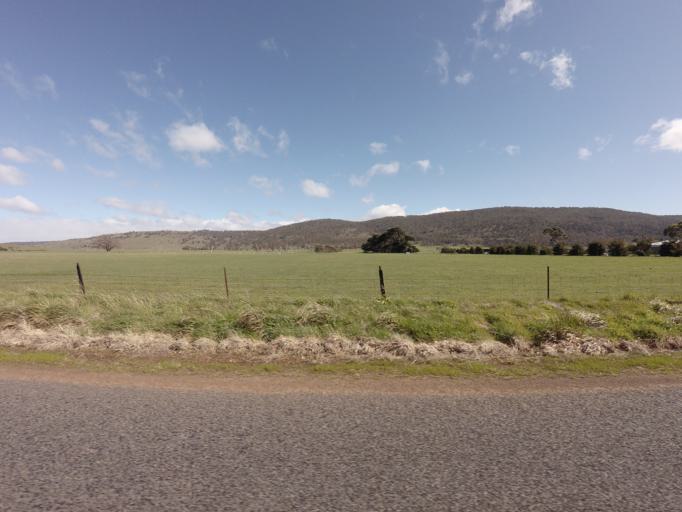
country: AU
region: Tasmania
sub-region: Northern Midlands
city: Evandale
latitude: -41.9838
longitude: 147.4499
